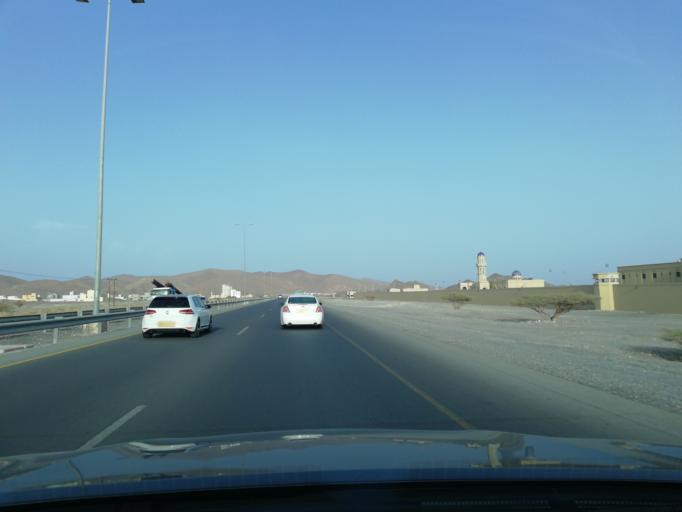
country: OM
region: Muhafazat ad Dakhiliyah
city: Izki
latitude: 22.8914
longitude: 57.6650
